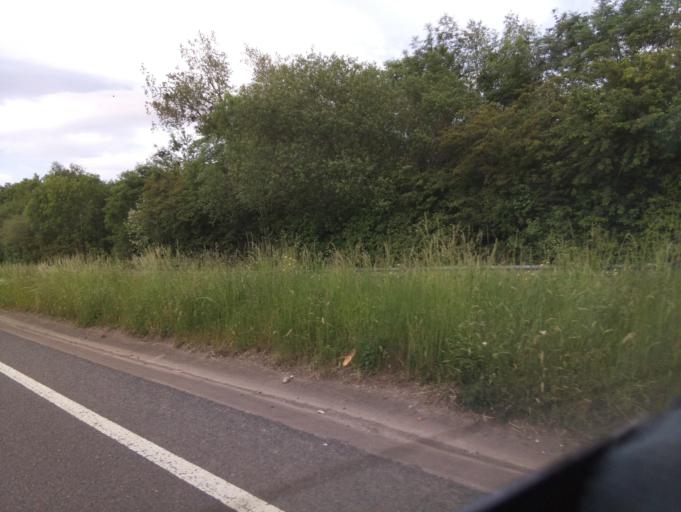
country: GB
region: England
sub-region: Worcestershire
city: Worcester
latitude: 52.1728
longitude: -2.2496
